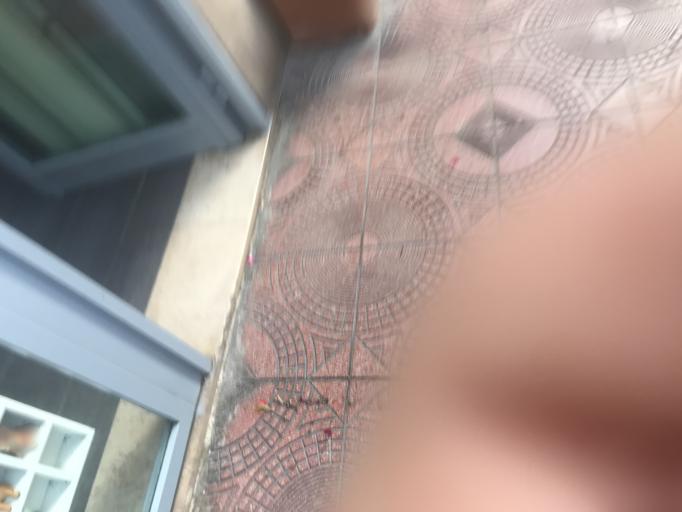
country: IT
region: Campania
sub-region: Provincia di Napoli
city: Napoli
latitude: 40.8617
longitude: 14.2168
